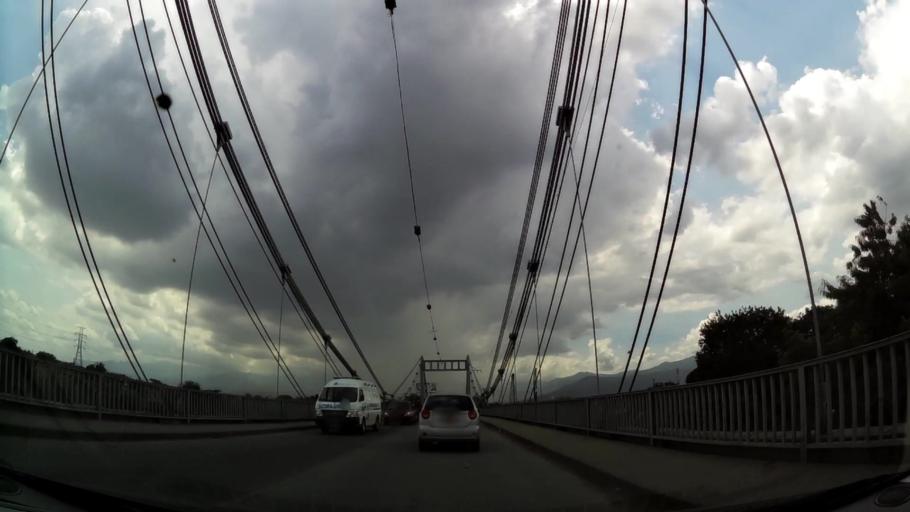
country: CO
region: Valle del Cauca
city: Cali
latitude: 3.4505
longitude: -76.4755
